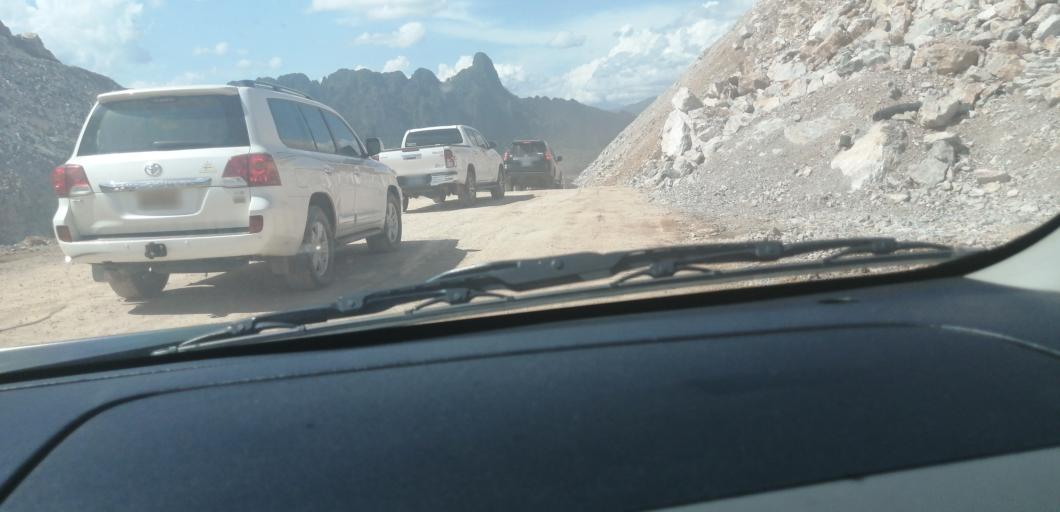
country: LA
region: Vientiane
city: Vangviang
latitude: 18.8702
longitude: 102.4280
